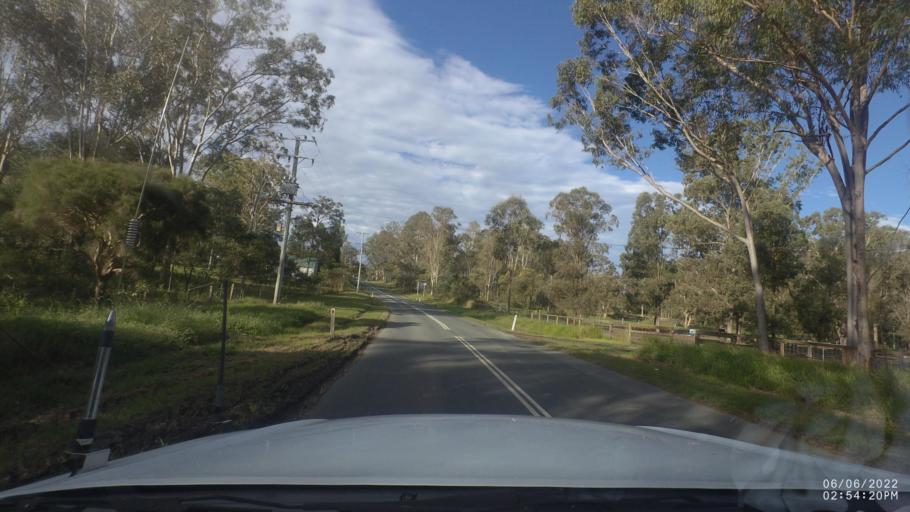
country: AU
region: Queensland
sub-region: Logan
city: Cedar Vale
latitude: -27.8552
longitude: 153.0483
